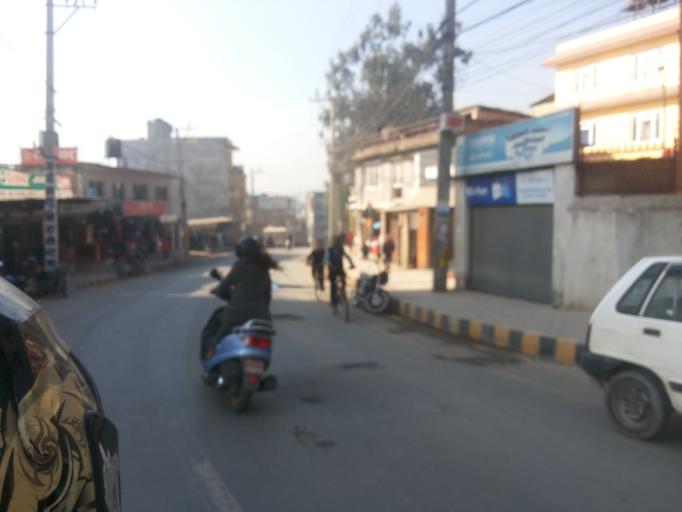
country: NP
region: Central Region
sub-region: Bagmati Zone
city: Kathmandu
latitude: 27.6856
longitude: 85.3351
